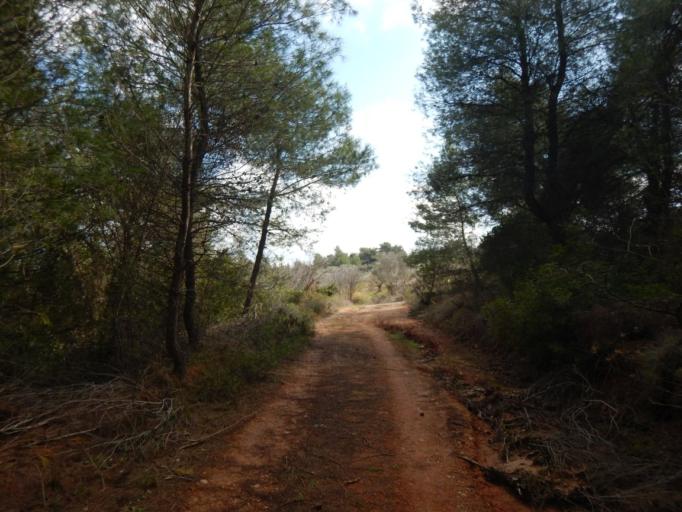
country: GR
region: Attica
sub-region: Nomarchia Anatolikis Attikis
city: Markopoulo Oropou
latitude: 38.2970
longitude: 23.8327
